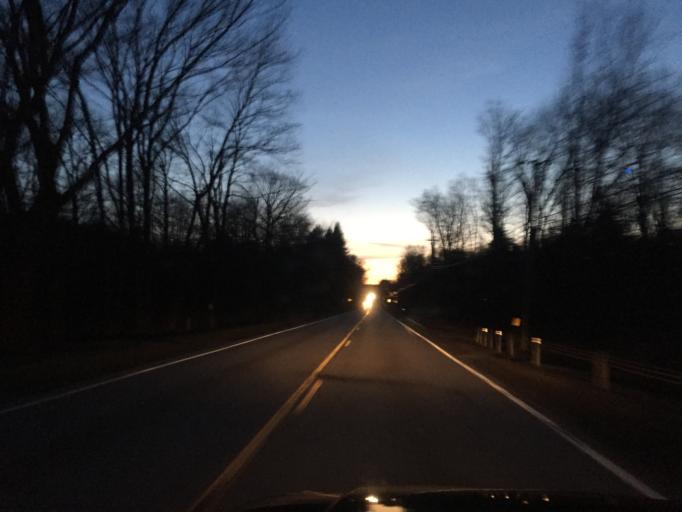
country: US
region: Connecticut
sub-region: Windham County
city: South Woodstock
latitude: 41.8599
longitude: -72.0247
